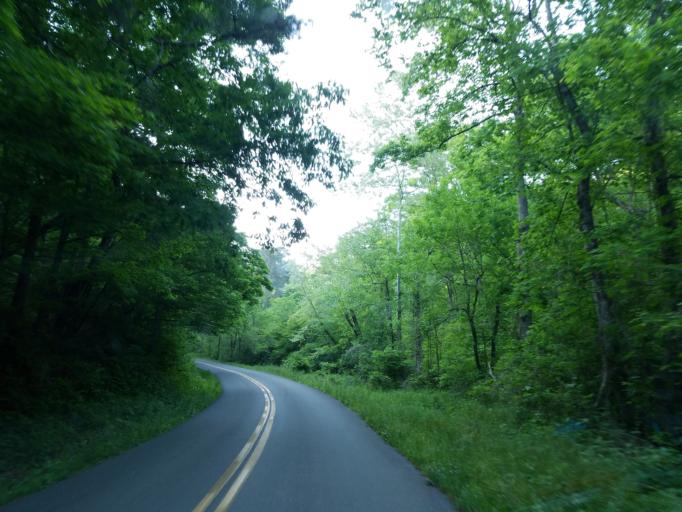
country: US
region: Georgia
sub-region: Gordon County
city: Calhoun
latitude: 34.5772
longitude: -85.0980
